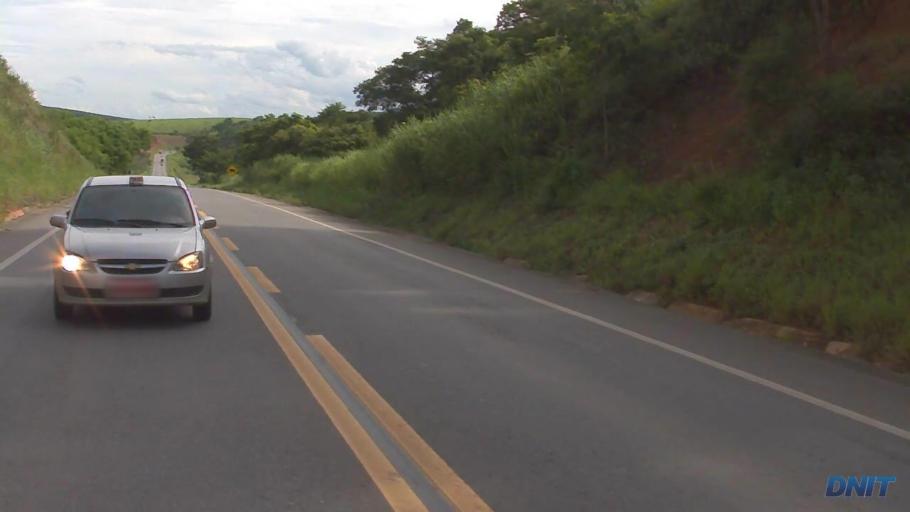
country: BR
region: Minas Gerais
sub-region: Belo Oriente
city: Belo Oriente
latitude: -19.2555
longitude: -42.3412
